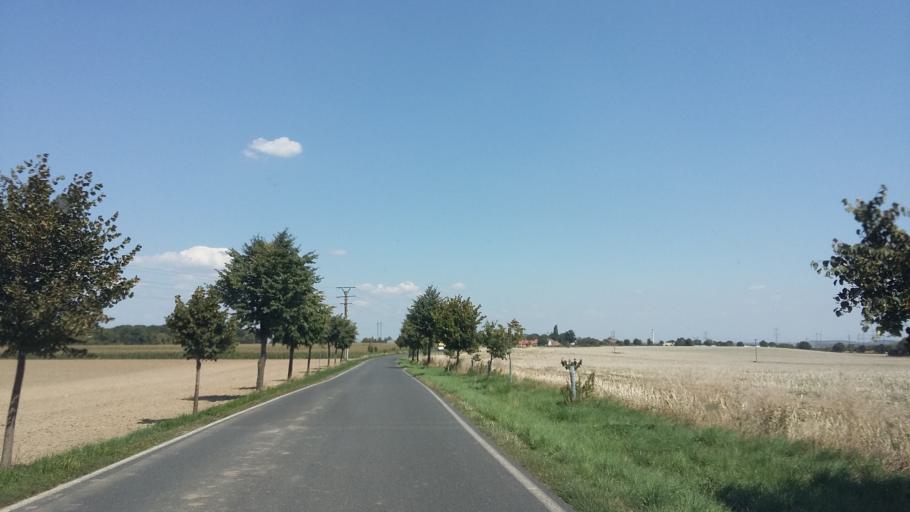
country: CZ
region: Central Bohemia
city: Zelenec
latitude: 50.1376
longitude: 14.6816
